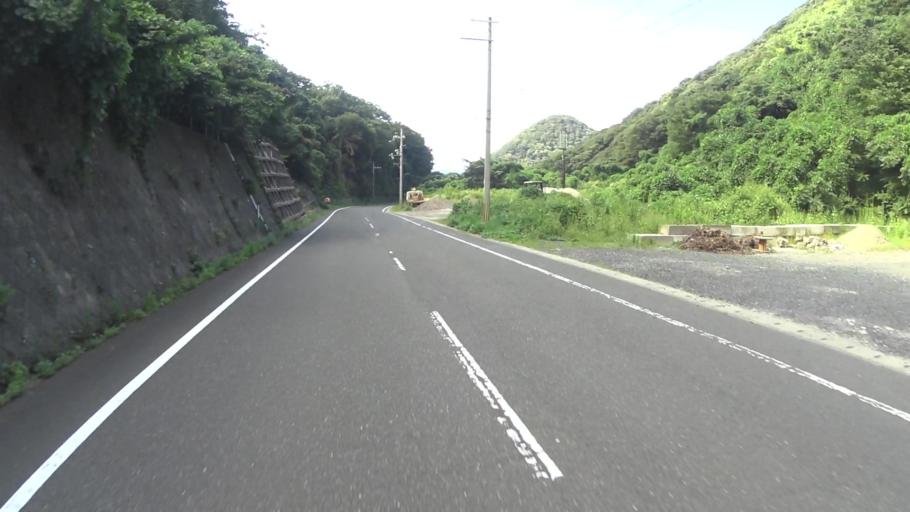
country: JP
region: Kyoto
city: Miyazu
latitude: 35.7673
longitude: 135.2285
